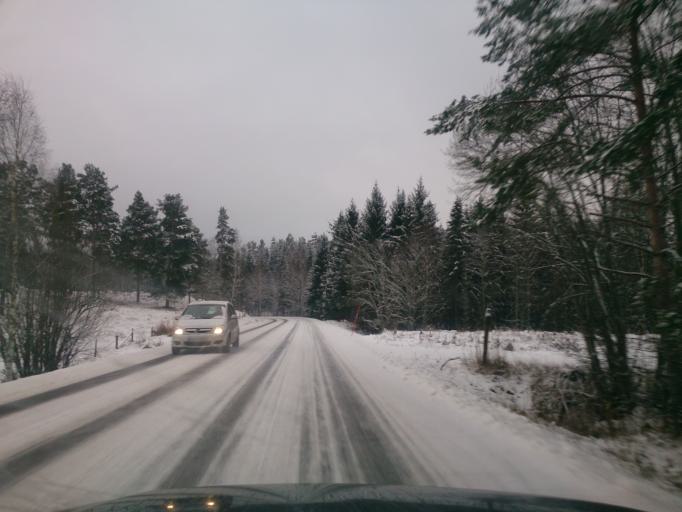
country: SE
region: OEstergoetland
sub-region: Atvidabergs Kommun
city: Atvidaberg
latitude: 58.3586
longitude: 16.0314
